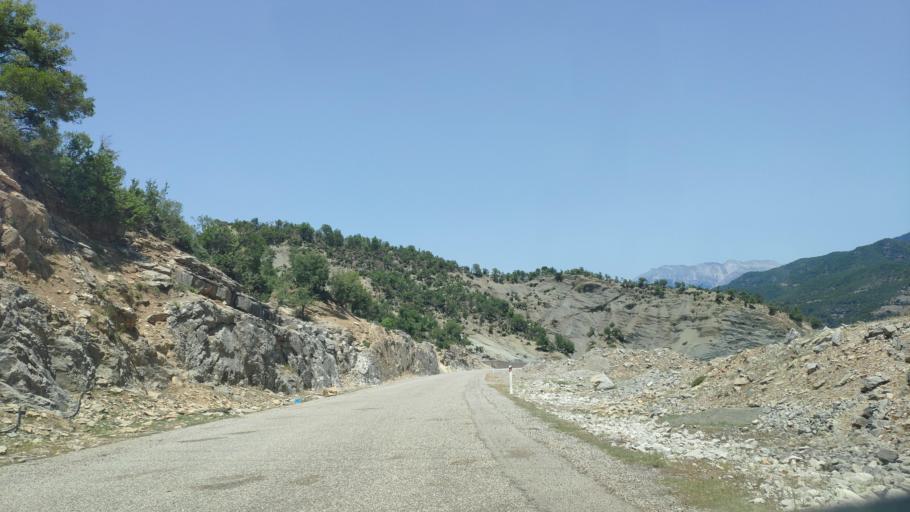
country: GR
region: Thessaly
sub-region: Nomos Kardhitsas
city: Anthiro
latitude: 39.1550
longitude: 21.3836
